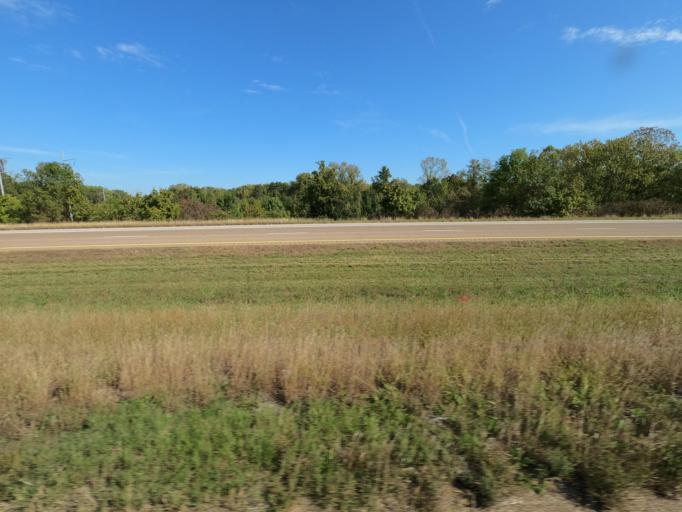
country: US
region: Tennessee
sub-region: Shelby County
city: Millington
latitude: 35.3295
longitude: -89.8915
